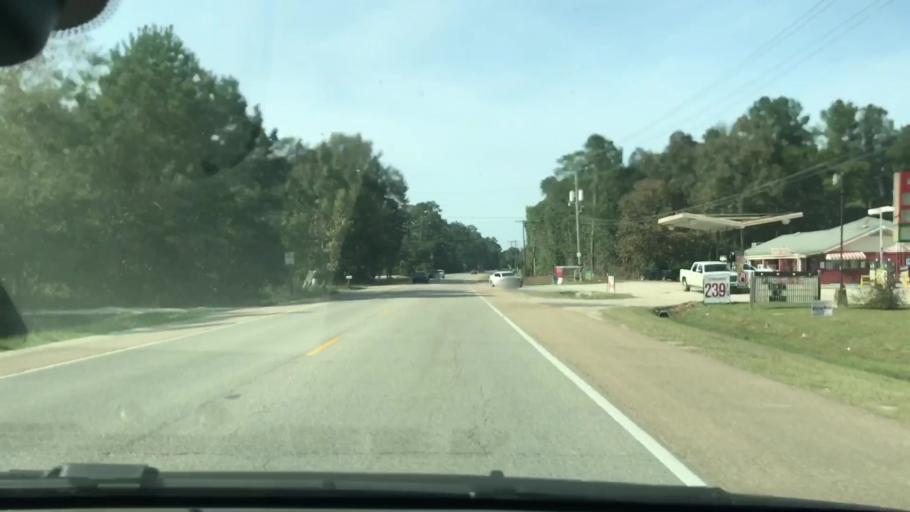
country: US
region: Louisiana
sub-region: Saint Tammany Parish
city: Pearl River
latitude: 30.4115
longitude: -89.7790
